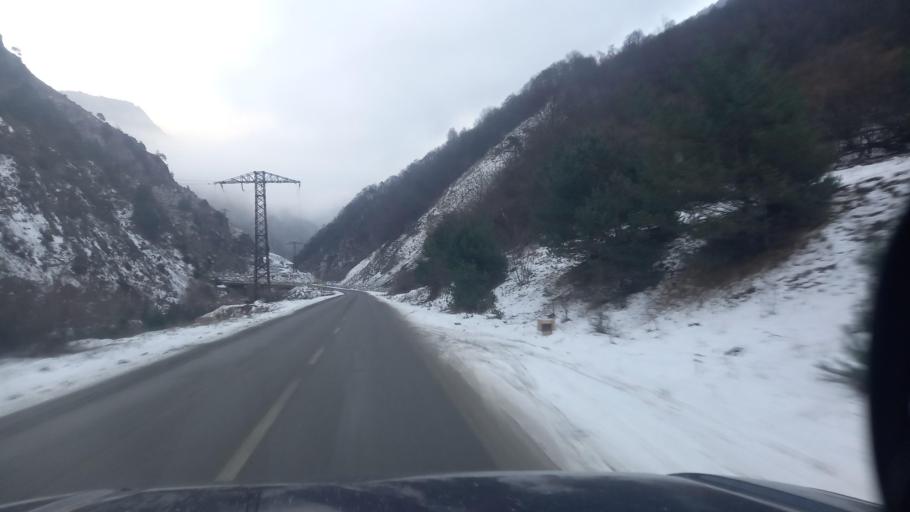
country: RU
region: Ingushetiya
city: Dzhayrakh
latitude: 42.7909
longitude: 44.7694
